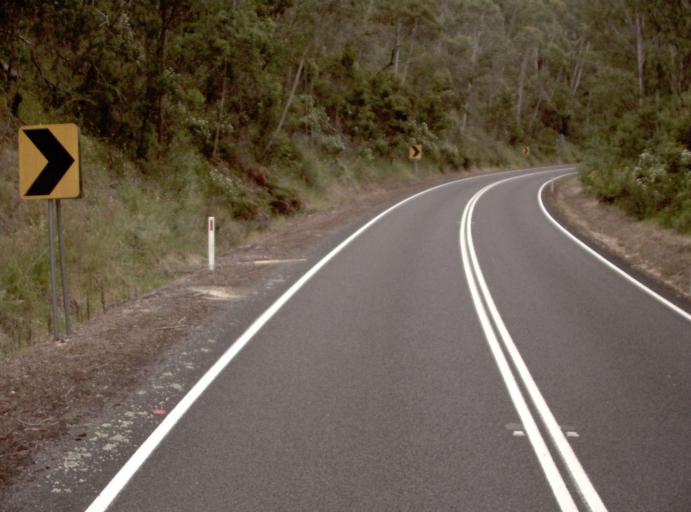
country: AU
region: New South Wales
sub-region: Bombala
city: Bombala
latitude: -37.3598
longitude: 149.2004
